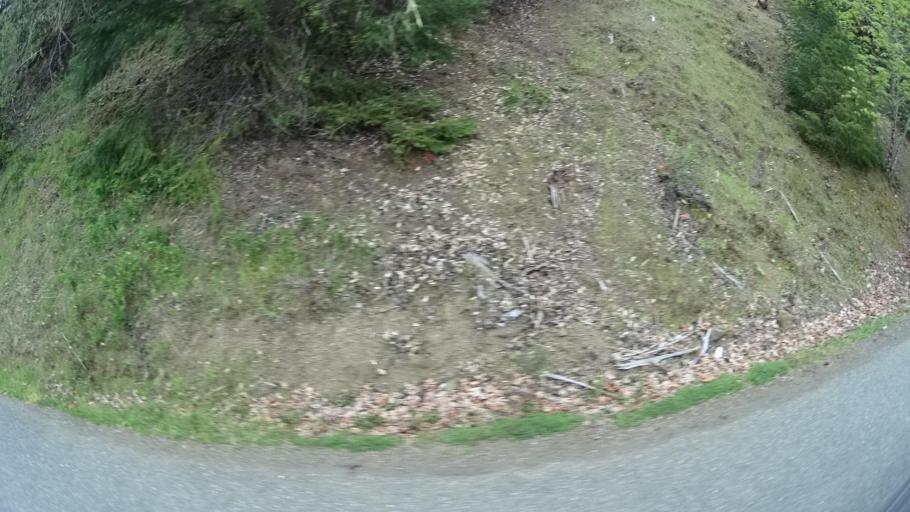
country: US
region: California
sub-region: Humboldt County
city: Redway
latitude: 40.1580
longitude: -123.5568
